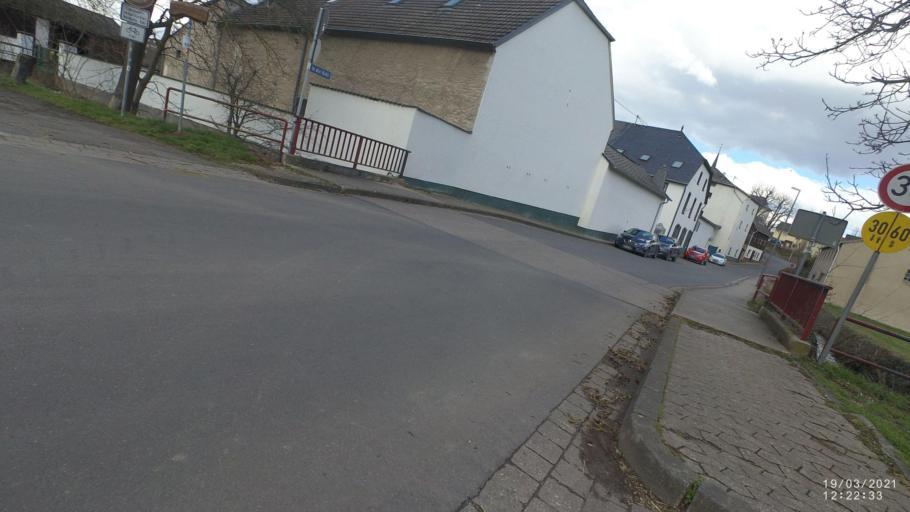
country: DE
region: Rheinland-Pfalz
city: Kretz
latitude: 50.3932
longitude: 7.3621
